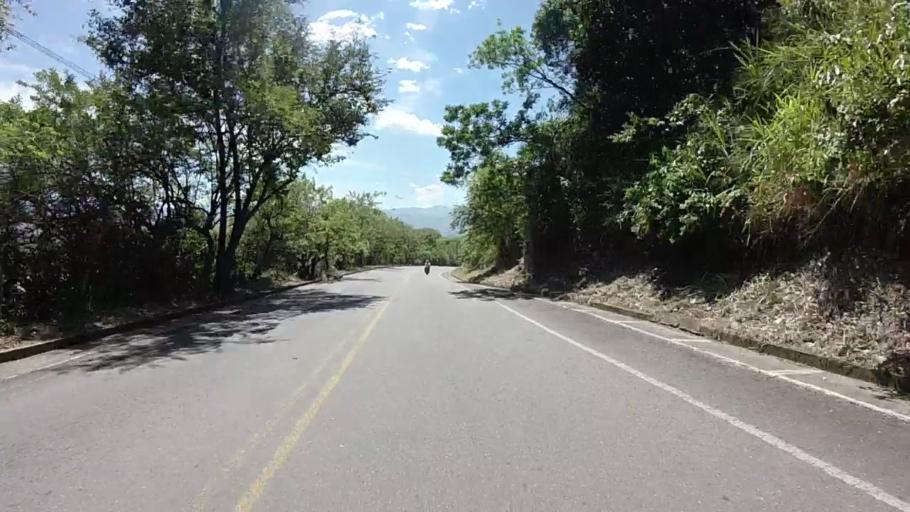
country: CO
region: Valle del Cauca
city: Cartago
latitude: 4.7329
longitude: -75.8948
